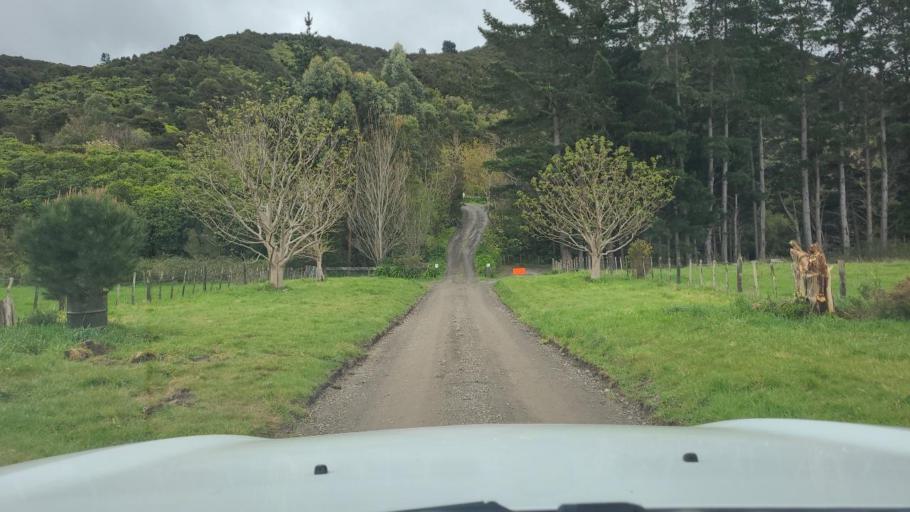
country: NZ
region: Wellington
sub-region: Upper Hutt City
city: Upper Hutt
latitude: -41.1176
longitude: 175.3099
